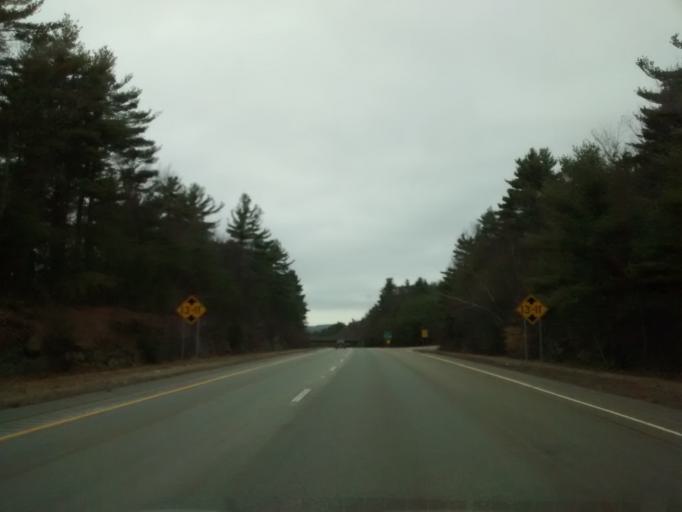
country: US
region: Massachusetts
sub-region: Worcester County
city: Templeton
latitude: 42.5693
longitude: -72.0685
